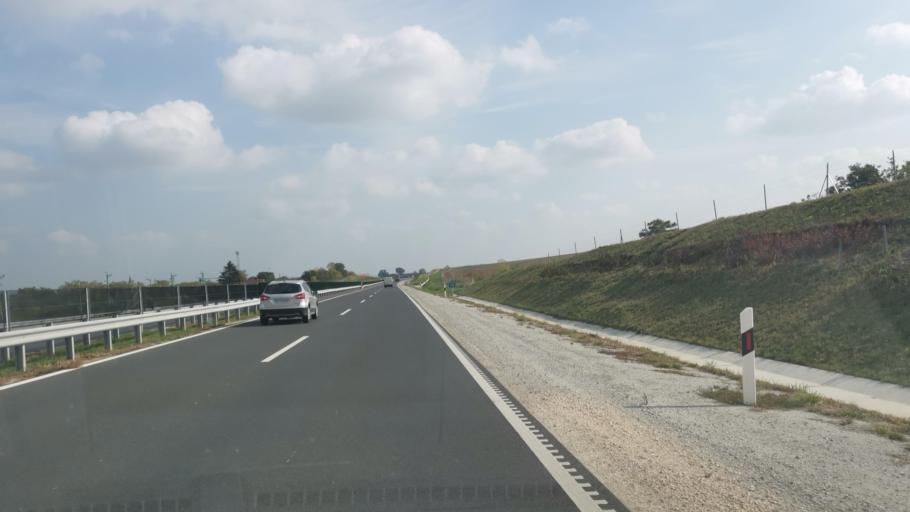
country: HU
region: Gyor-Moson-Sopron
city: Nagycenk
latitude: 47.6026
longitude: 16.6819
